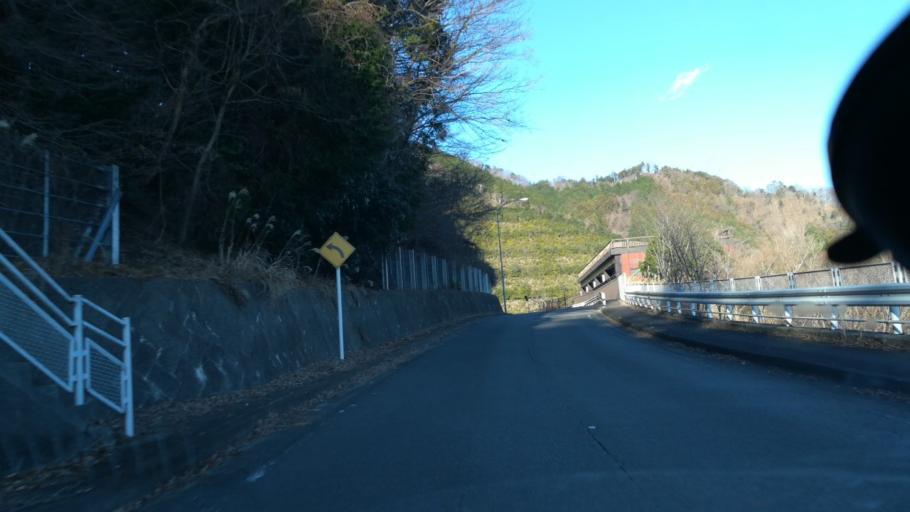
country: JP
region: Tokyo
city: Hachioji
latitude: 35.5417
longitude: 139.2424
